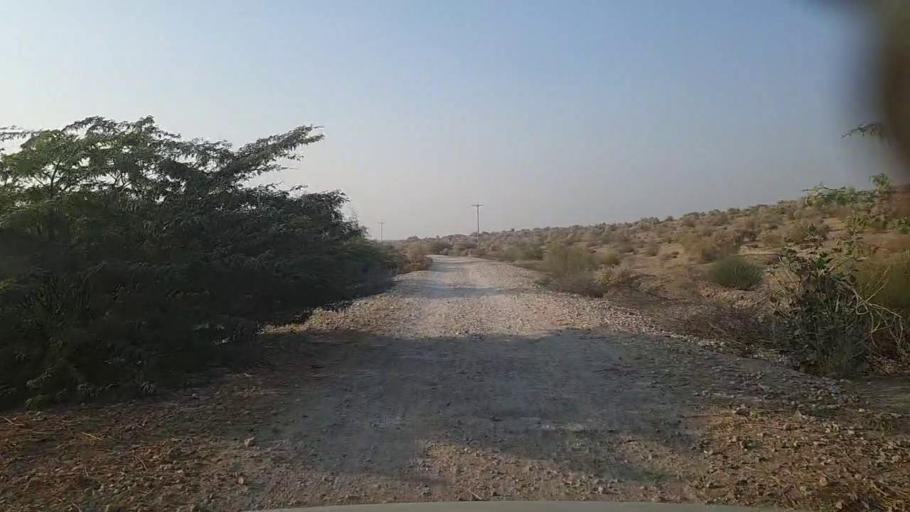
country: PK
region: Sindh
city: Pad Idan
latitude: 26.7201
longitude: 68.4555
